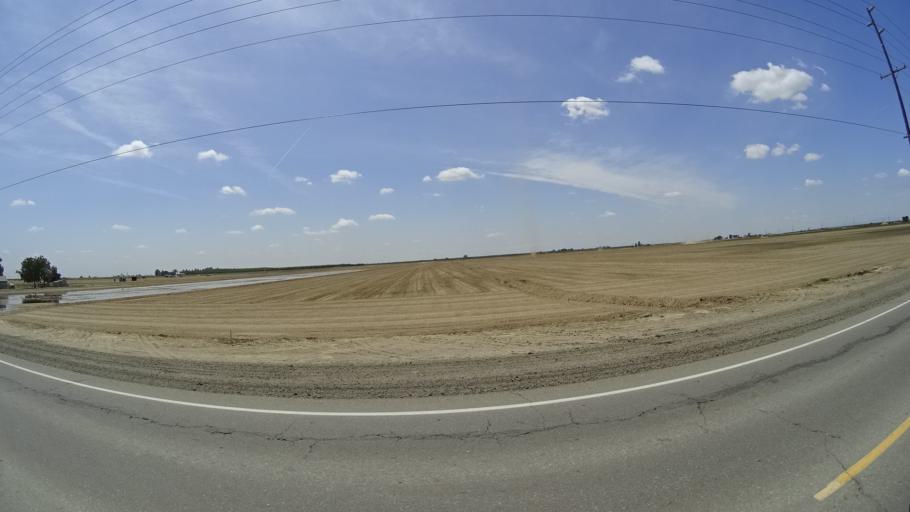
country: US
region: California
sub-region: Kings County
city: Home Garden
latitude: 36.2986
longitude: -119.5747
